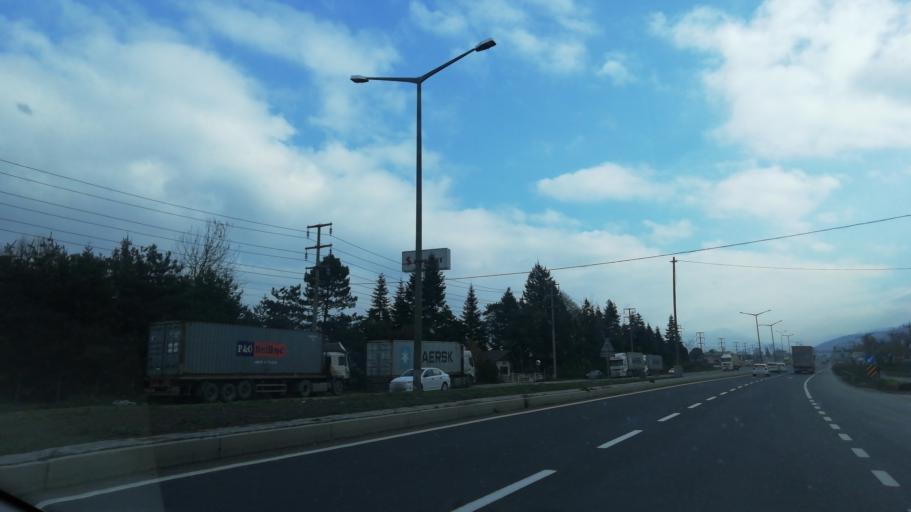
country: TR
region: Duzce
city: Kaynasli
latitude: 40.7783
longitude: 31.2906
